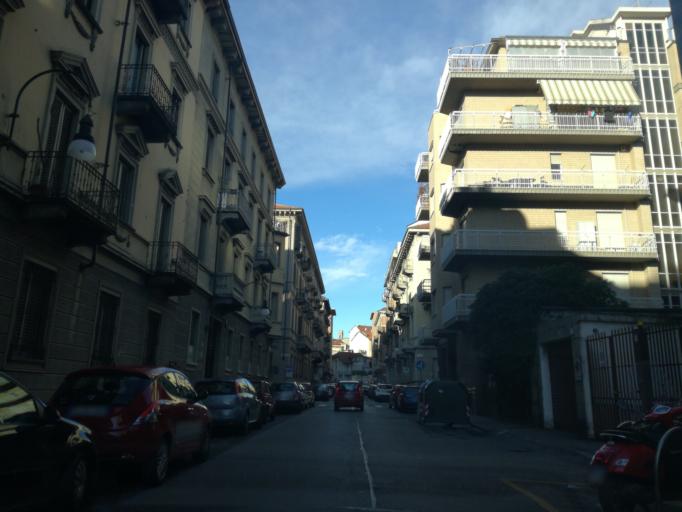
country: IT
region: Piedmont
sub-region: Provincia di Torino
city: Turin
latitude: 45.0746
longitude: 7.6658
